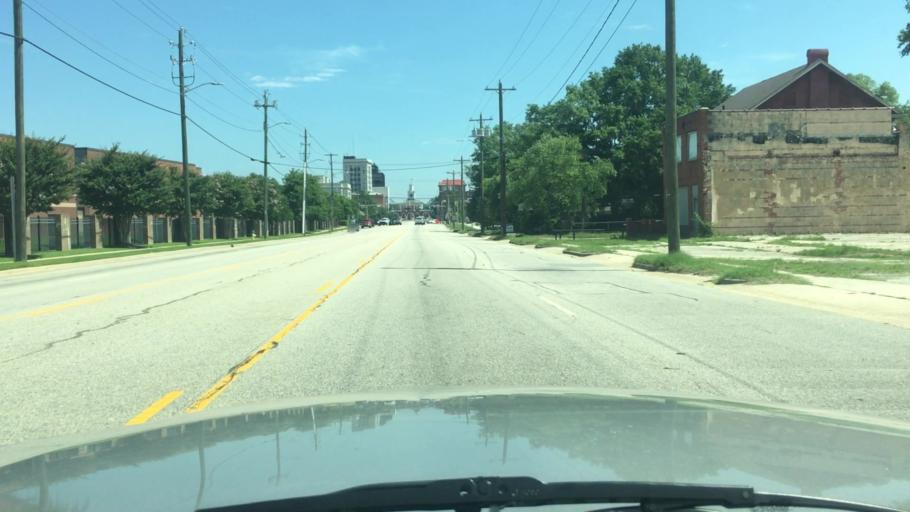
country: US
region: North Carolina
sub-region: Cumberland County
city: Fayetteville
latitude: 35.0479
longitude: -78.8799
